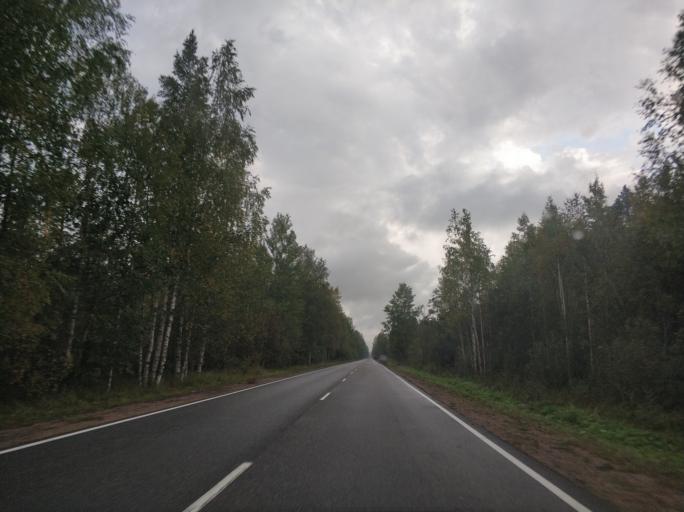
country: RU
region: Leningrad
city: Borisova Griva
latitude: 60.1428
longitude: 30.9485
